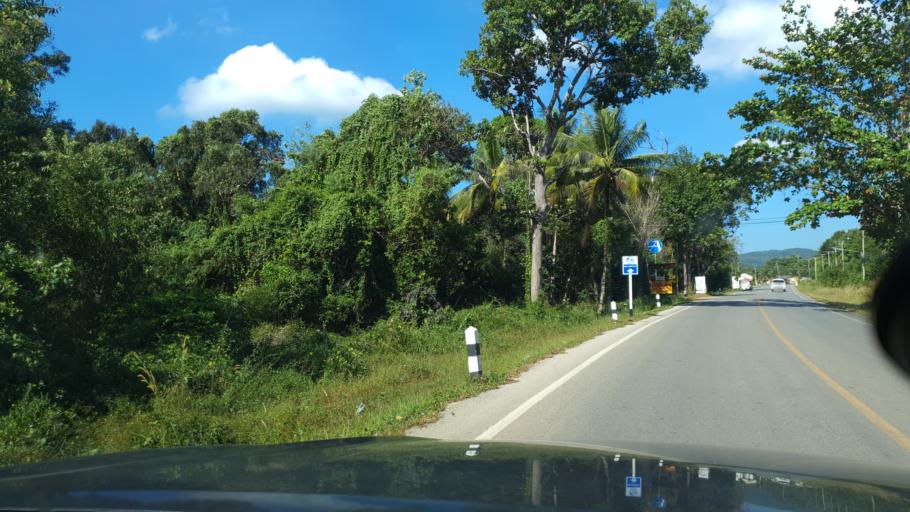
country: TH
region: Krabi
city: Krabi
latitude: 8.0279
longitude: 98.8715
